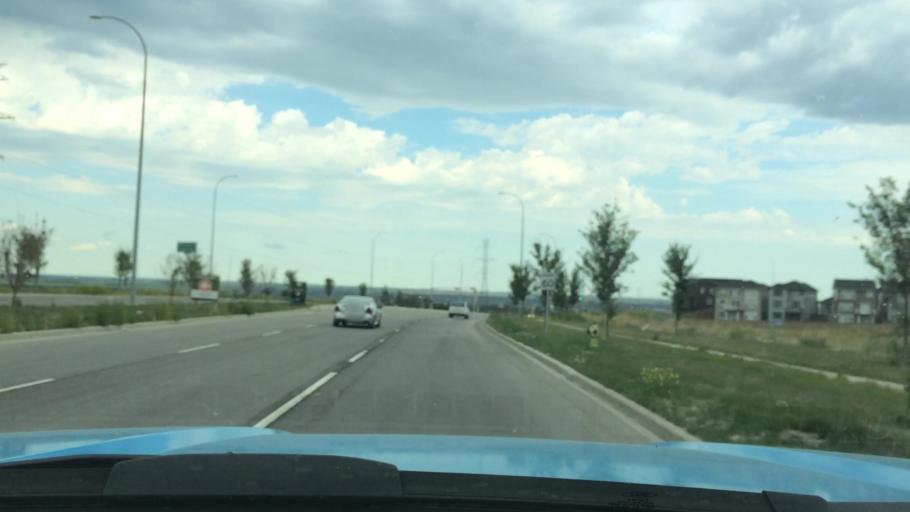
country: CA
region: Alberta
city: Calgary
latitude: 51.1676
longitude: -114.1637
